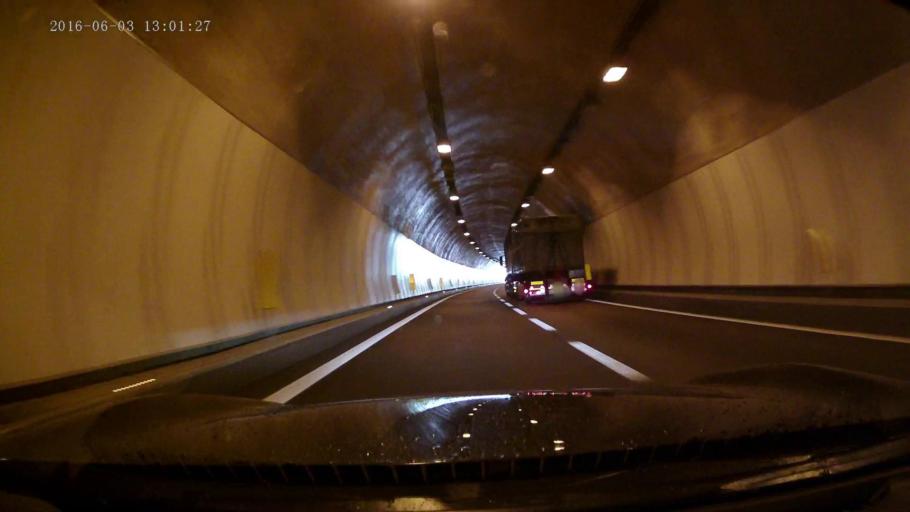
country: IT
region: Trentino-Alto Adige
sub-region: Bolzano
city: Fortezza
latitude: 46.7871
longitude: 11.6149
